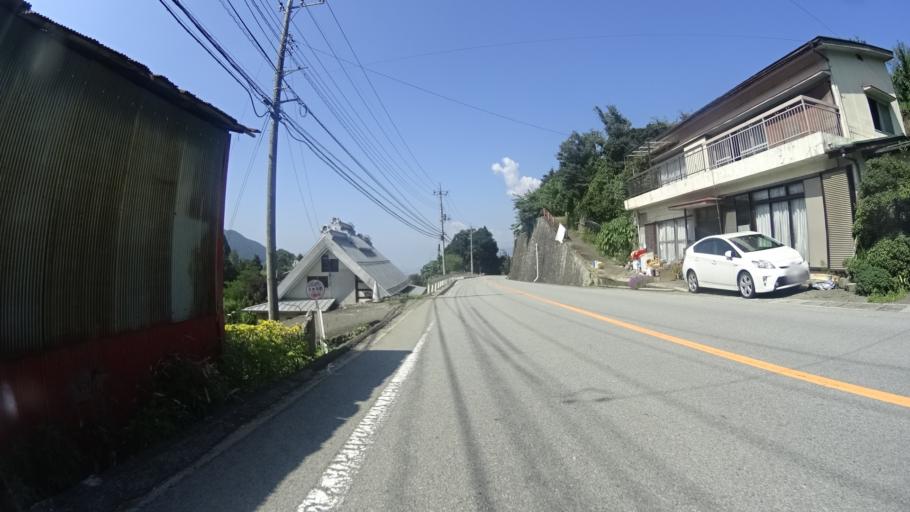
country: JP
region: Yamanashi
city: Enzan
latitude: 35.7322
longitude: 138.7817
